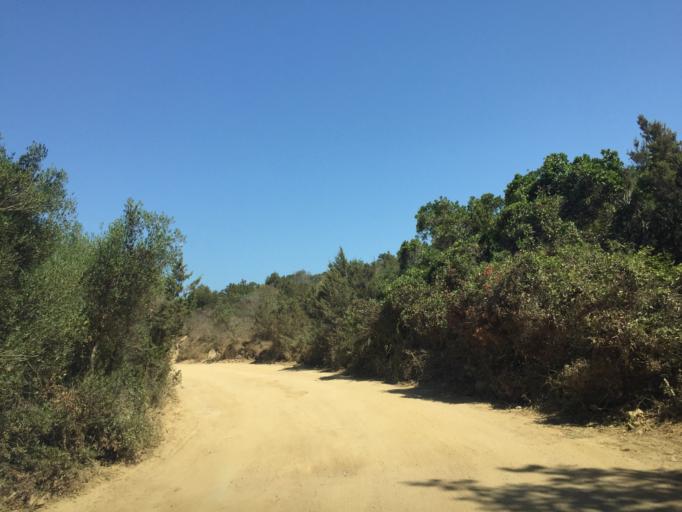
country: IT
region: Sardinia
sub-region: Provincia di Olbia-Tempio
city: San Teodoro
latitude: 40.8396
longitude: 9.7185
